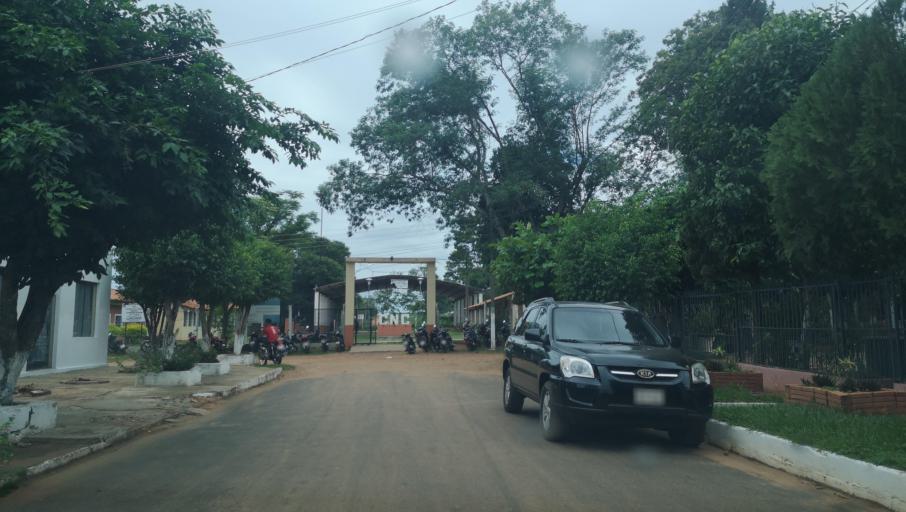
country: PY
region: San Pedro
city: Capiibary
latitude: -24.7406
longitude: -56.0235
